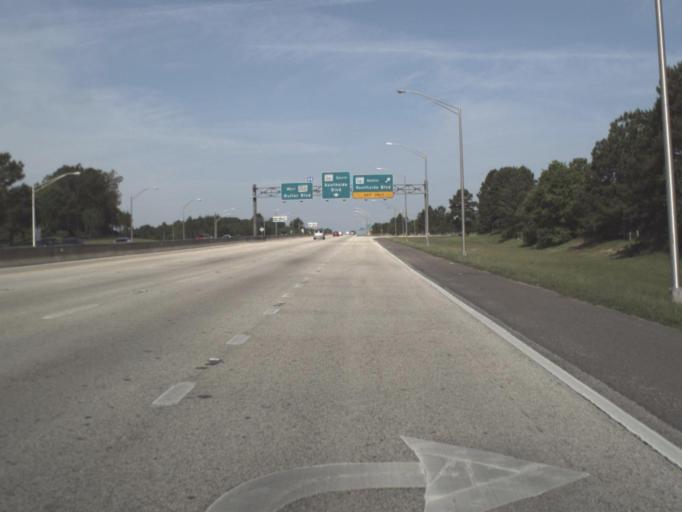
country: US
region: Florida
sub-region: Duval County
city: Jacksonville
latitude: 30.2501
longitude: -81.5451
